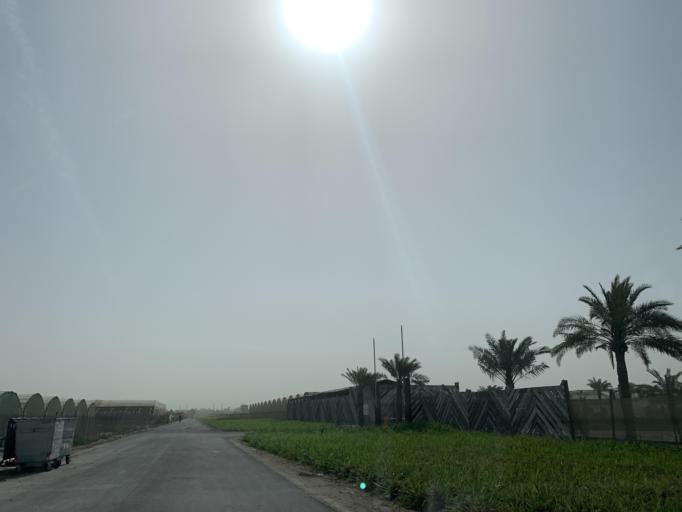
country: BH
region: Northern
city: Madinat `Isa
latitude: 26.1723
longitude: 50.5272
